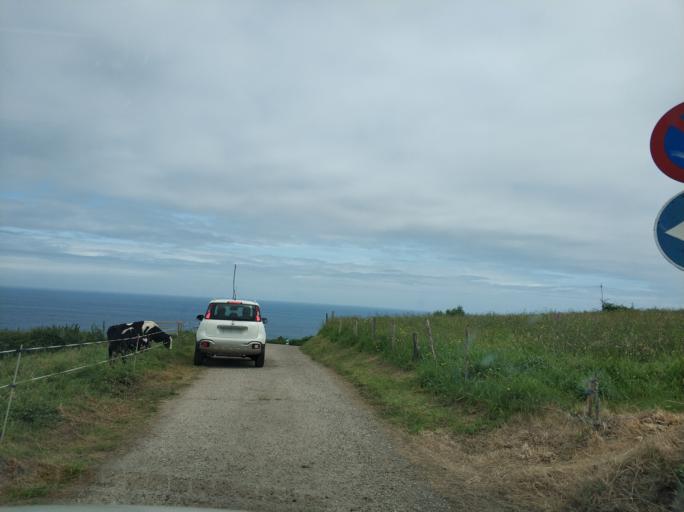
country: ES
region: Asturias
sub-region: Province of Asturias
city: Cudillero
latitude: 43.5641
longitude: -6.2981
